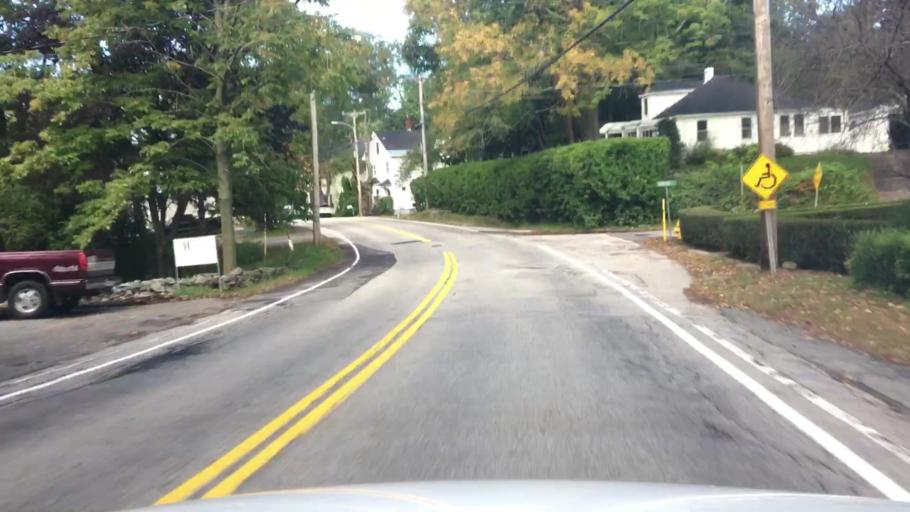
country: US
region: Maine
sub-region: York County
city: Kittery
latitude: 43.0861
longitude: -70.7256
